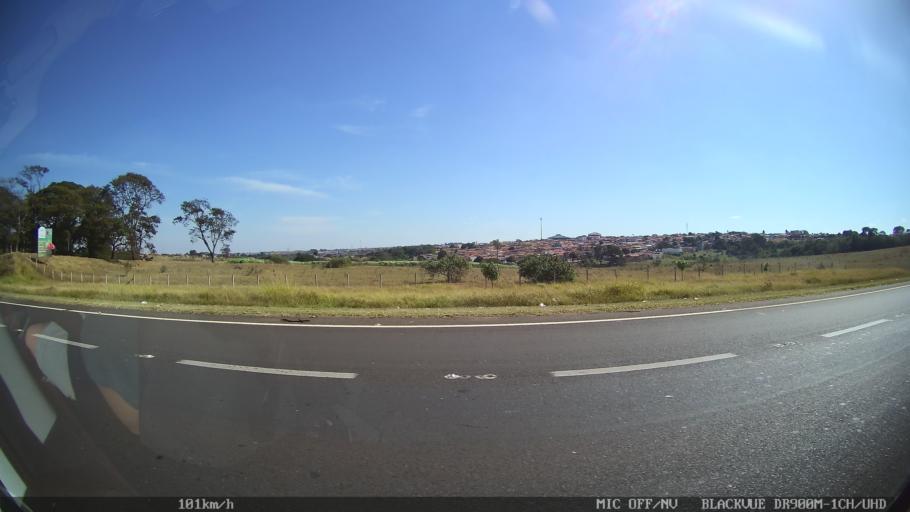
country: BR
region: Sao Paulo
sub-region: Franca
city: Franca
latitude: -20.5177
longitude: -47.4168
